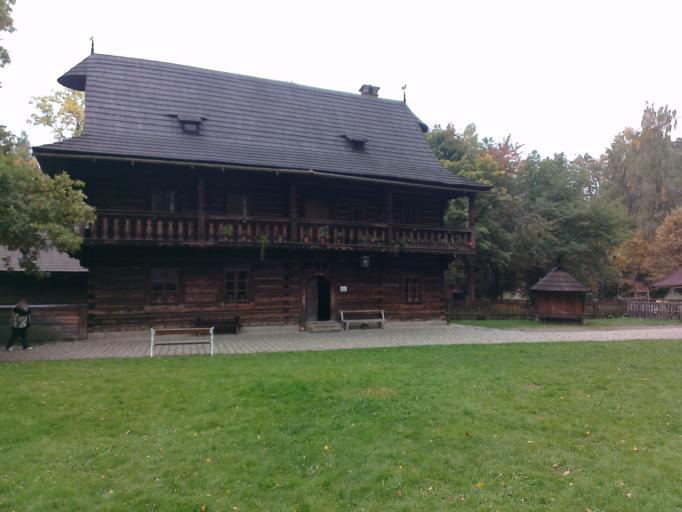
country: CZ
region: Zlin
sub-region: Okres Vsetin
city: Roznov pod Radhostem
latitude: 49.4625
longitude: 18.1486
